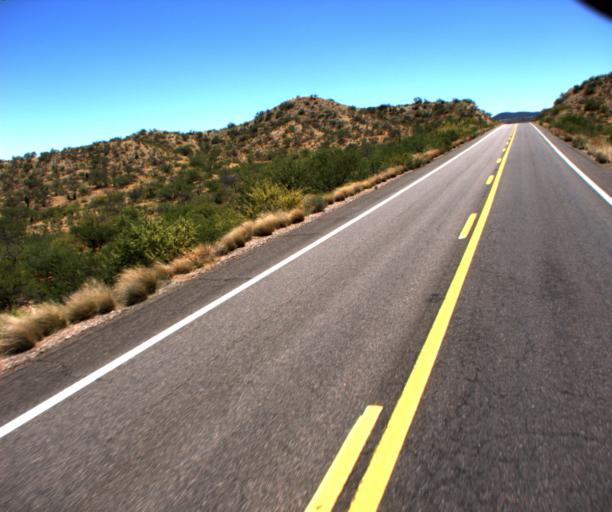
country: US
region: Arizona
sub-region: Gila County
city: Globe
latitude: 33.3664
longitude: -110.7371
